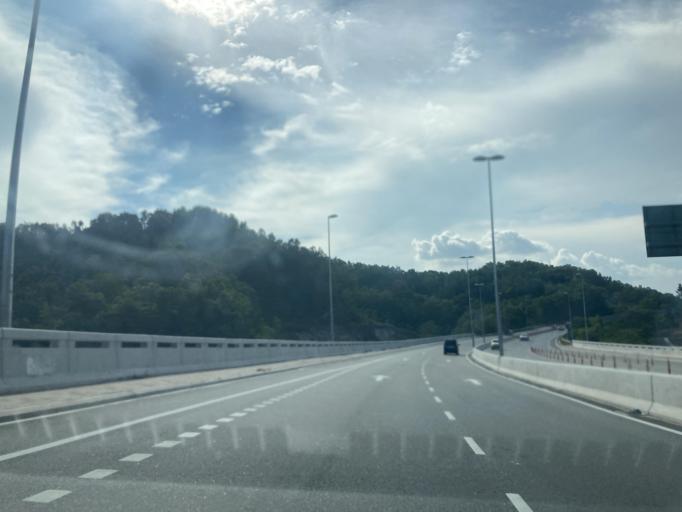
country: MY
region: Selangor
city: Kampung Baru Subang
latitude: 3.1352
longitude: 101.4888
